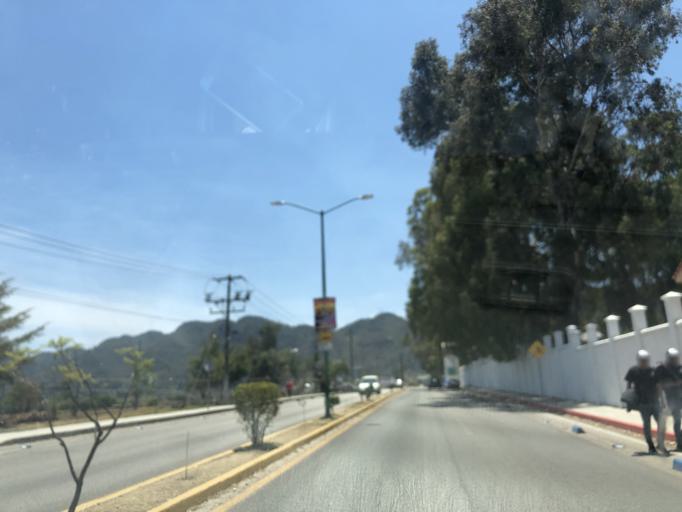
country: MX
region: Chiapas
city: San Cristobal de las Casas
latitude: 16.7266
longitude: -92.6514
